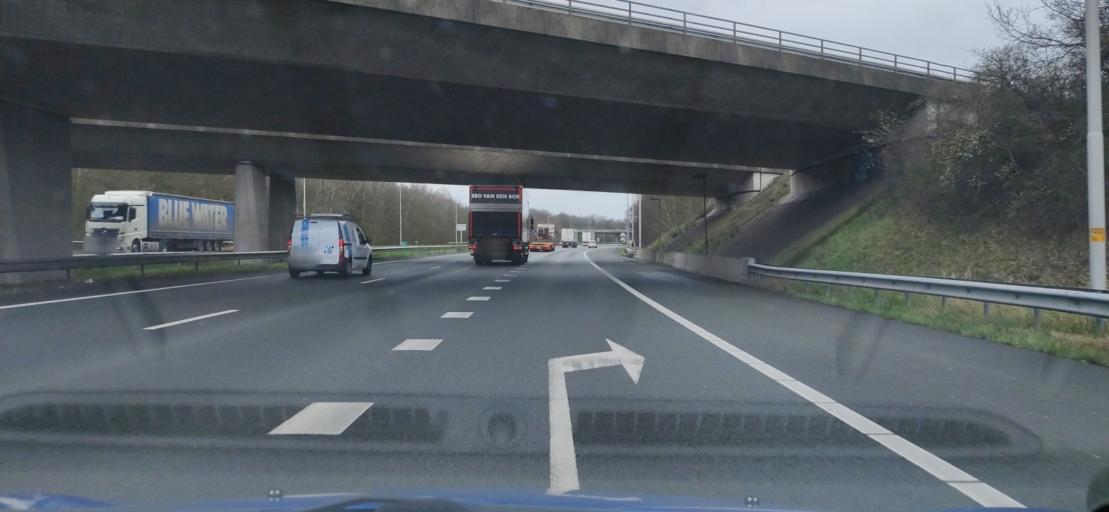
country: NL
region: Overijssel
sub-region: Gemeente Borne
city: Borne
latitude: 52.2855
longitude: 6.7438
